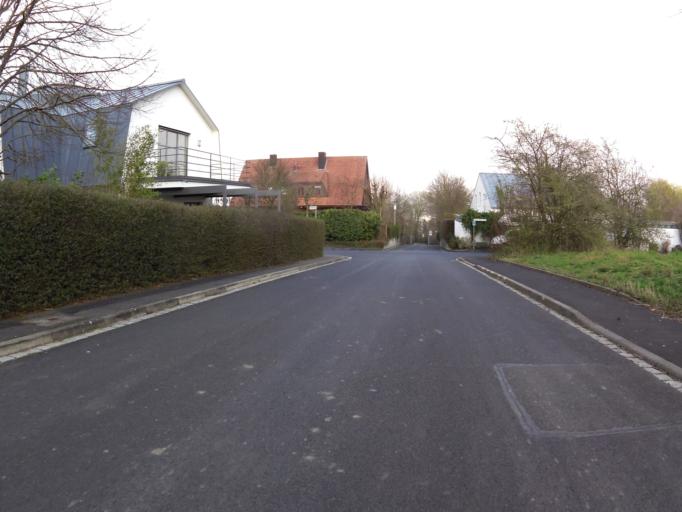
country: DE
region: Bavaria
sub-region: Regierungsbezirk Unterfranken
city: Kitzingen
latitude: 49.7453
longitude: 10.1557
